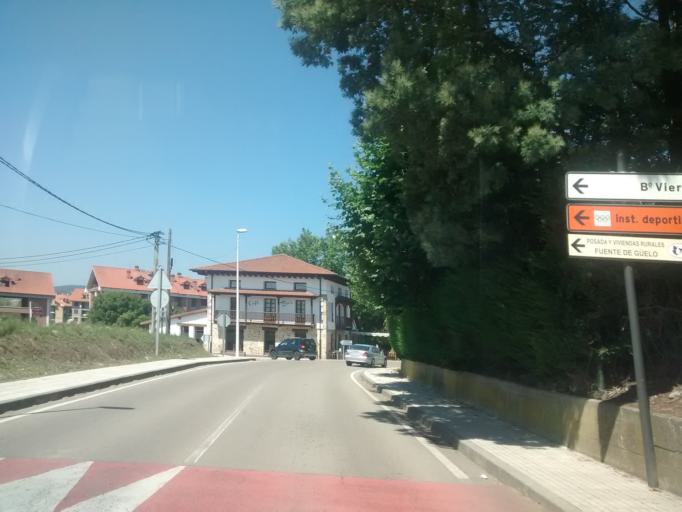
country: ES
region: Cantabria
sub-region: Provincia de Cantabria
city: San Miguel de Meruelo
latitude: 43.4548
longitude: -3.5749
